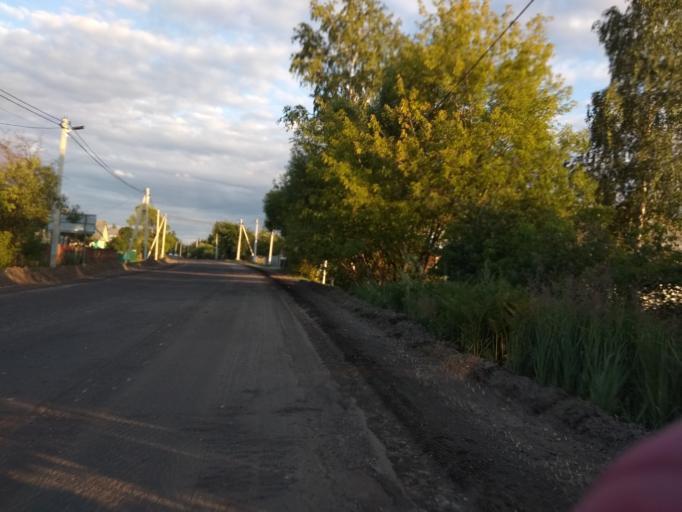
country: RU
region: Moskovskaya
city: Misheronskiy
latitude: 55.6550
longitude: 39.7523
